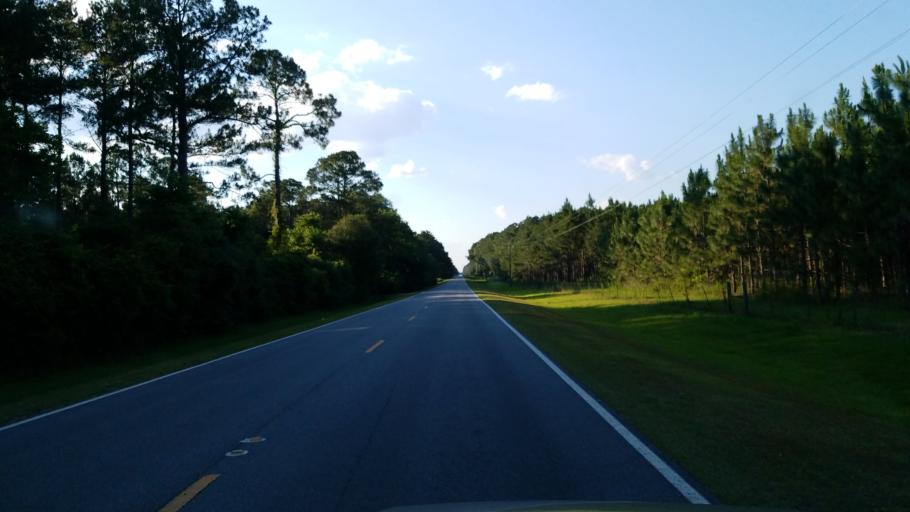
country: US
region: Georgia
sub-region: Lanier County
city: Lakeland
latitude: 31.0686
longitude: -83.0727
